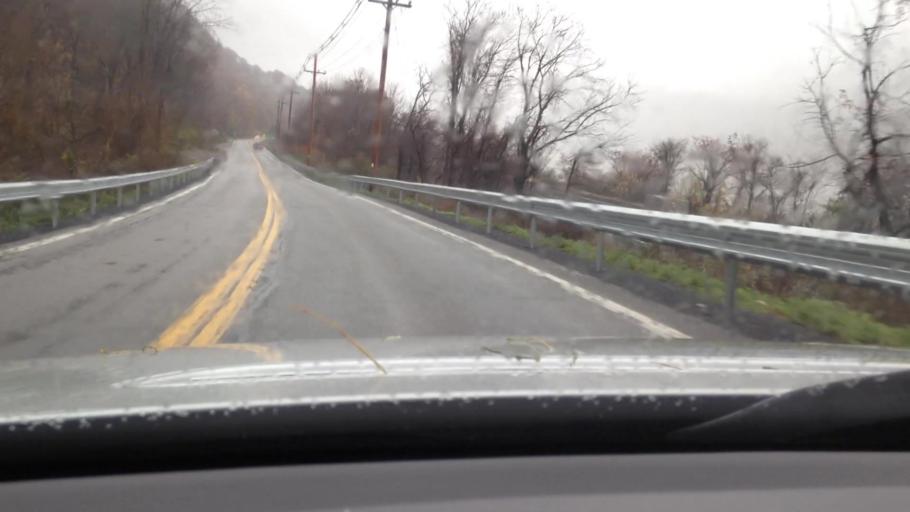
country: US
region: New York
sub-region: Orange County
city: Cornwall-on-Hudson
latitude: 41.4505
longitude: -73.9824
